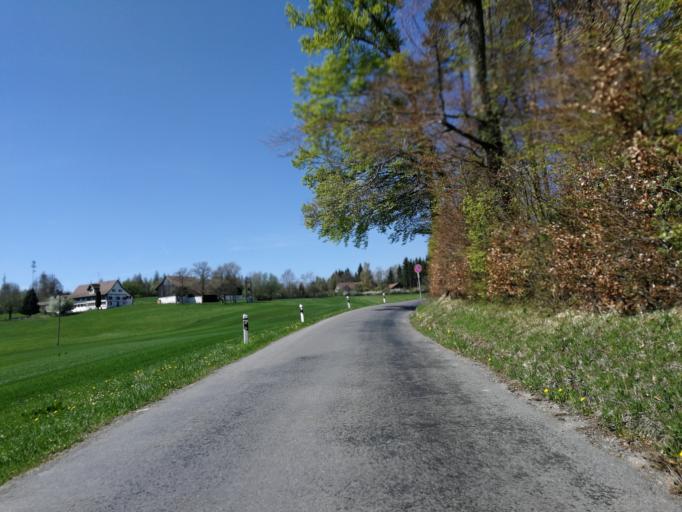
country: CH
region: Zurich
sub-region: Bezirk Uster
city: Aesch
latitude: 47.3111
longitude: 8.6601
